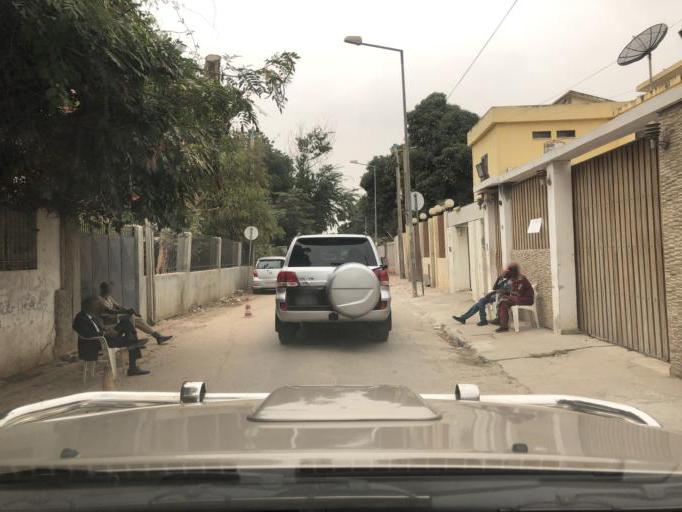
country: AO
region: Luanda
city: Luanda
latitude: -8.8199
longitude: 13.2497
